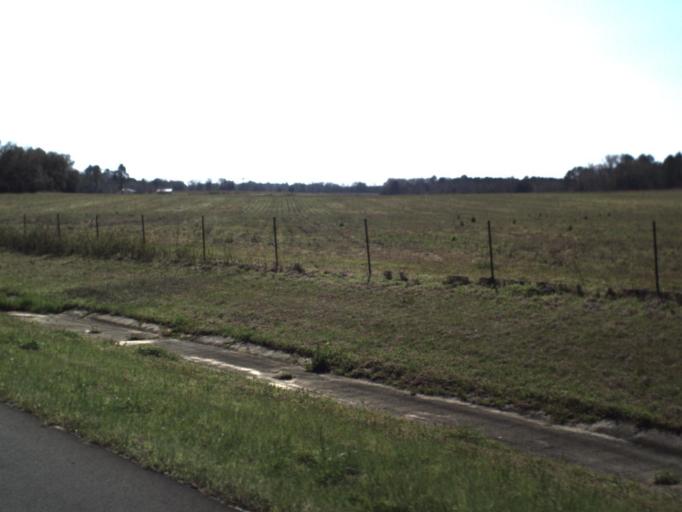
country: US
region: Florida
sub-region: Jackson County
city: Sneads
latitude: 30.8026
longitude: -85.0330
